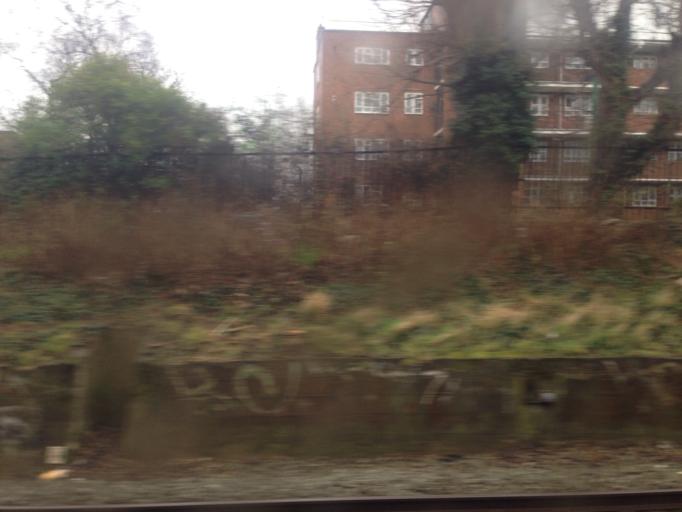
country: GB
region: England
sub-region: Greater London
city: Brixton Hill
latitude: 51.4276
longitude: -0.1386
